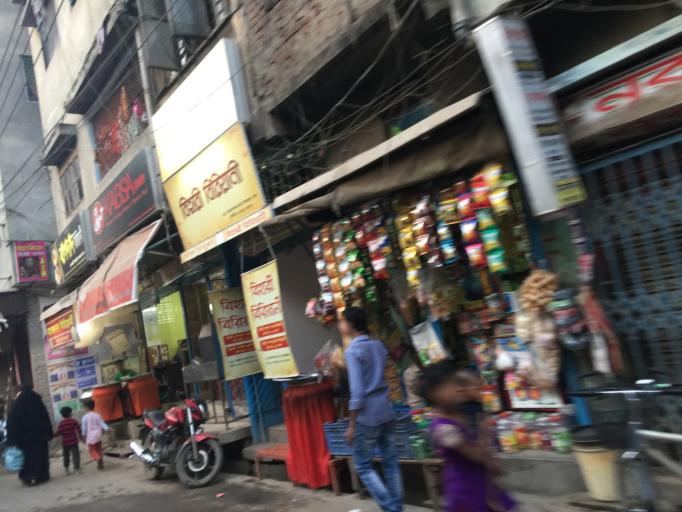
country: BD
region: Dhaka
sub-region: Dhaka
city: Dhaka
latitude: 23.7181
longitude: 90.4008
